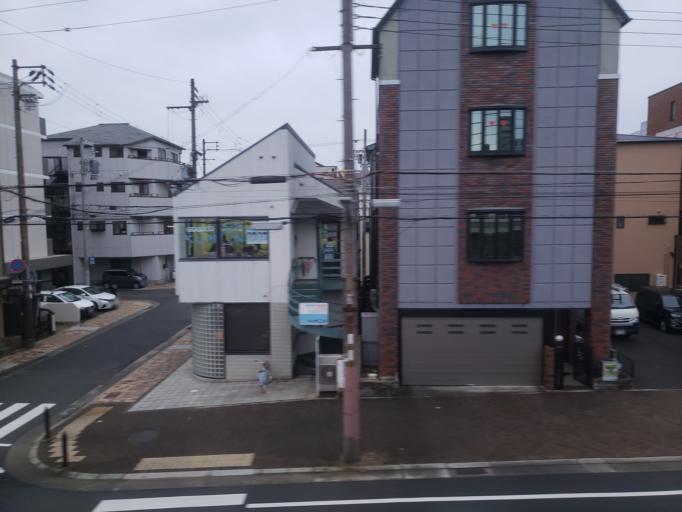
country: JP
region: Hyogo
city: Kobe
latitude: 34.6537
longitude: 135.1387
